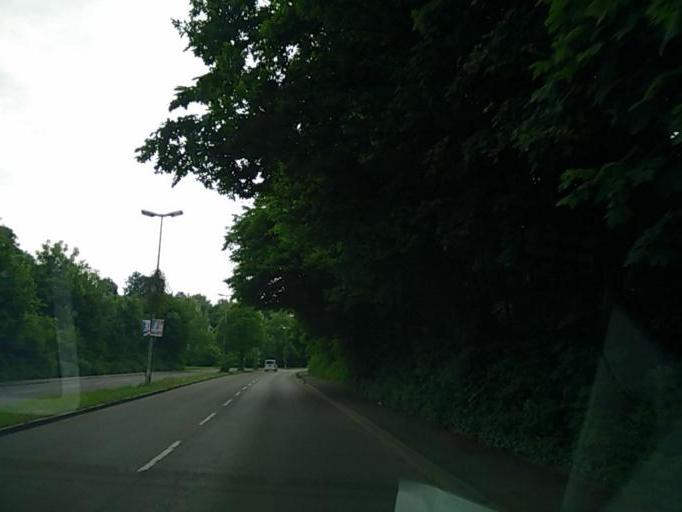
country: DE
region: Baden-Wuerttemberg
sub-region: Tuebingen Region
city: Tuebingen
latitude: 48.5326
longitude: 9.0677
